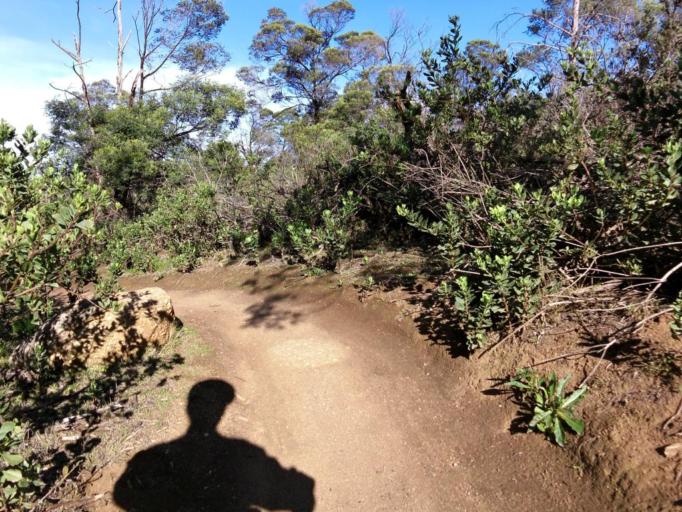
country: AU
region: Victoria
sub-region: Wyndham
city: Little River
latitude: -37.9256
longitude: 144.4332
